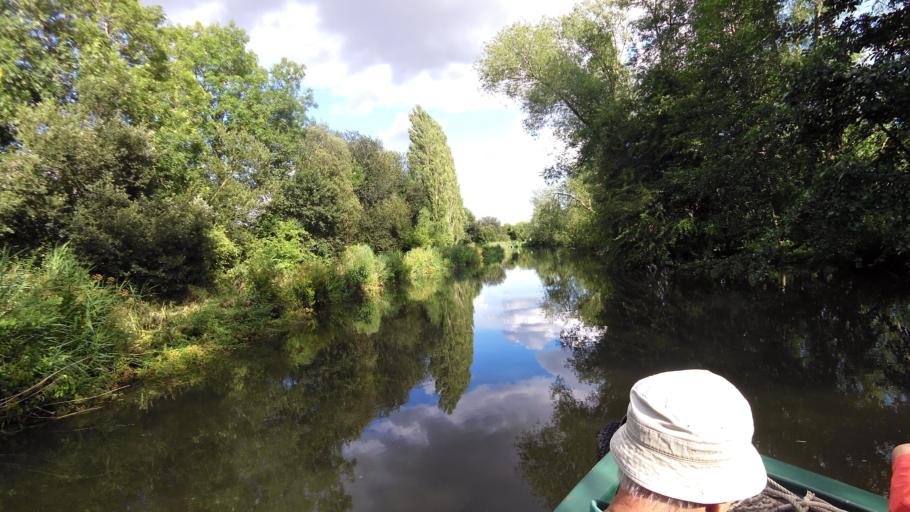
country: GB
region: England
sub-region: West Berkshire
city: Thatcham
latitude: 51.3943
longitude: -1.2779
